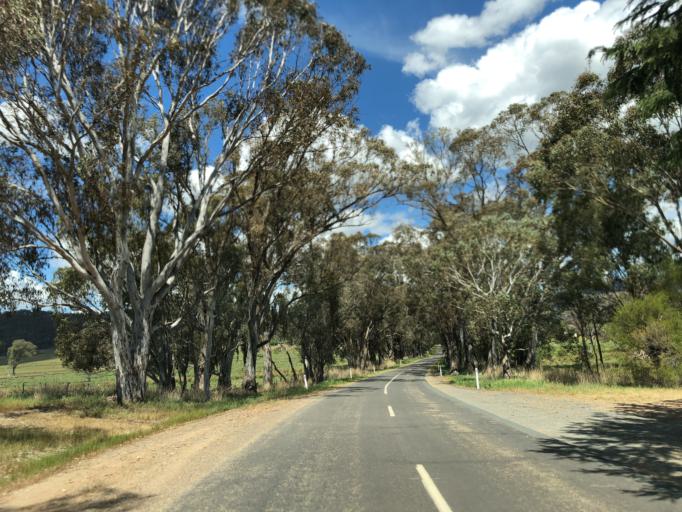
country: AU
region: Victoria
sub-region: Benalla
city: Benalla
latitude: -36.7451
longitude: 146.1181
